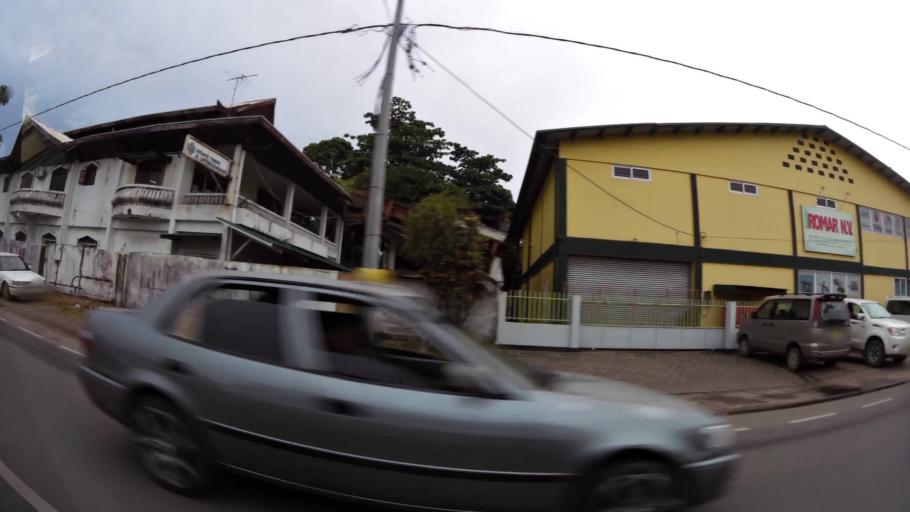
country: SR
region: Paramaribo
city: Paramaribo
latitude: 5.8045
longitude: -55.1822
